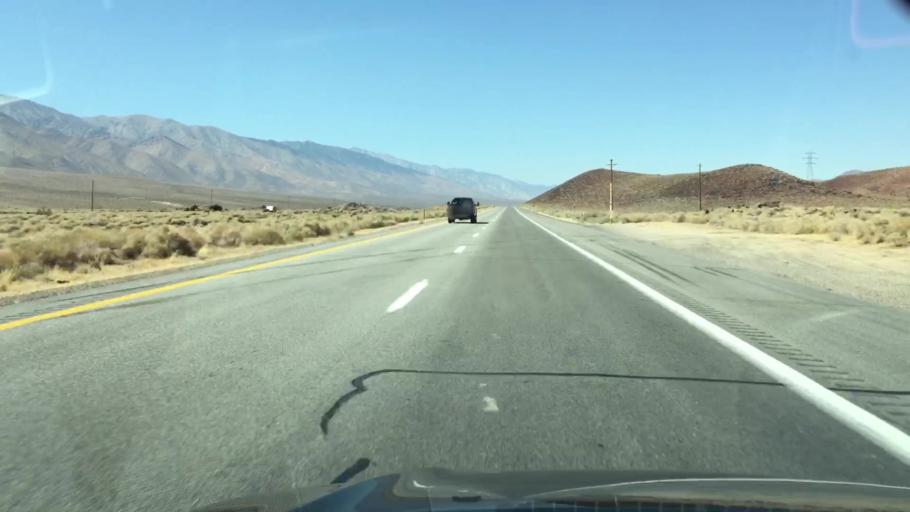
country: US
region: California
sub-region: Kern County
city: Inyokern
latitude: 35.9786
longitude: -117.9235
